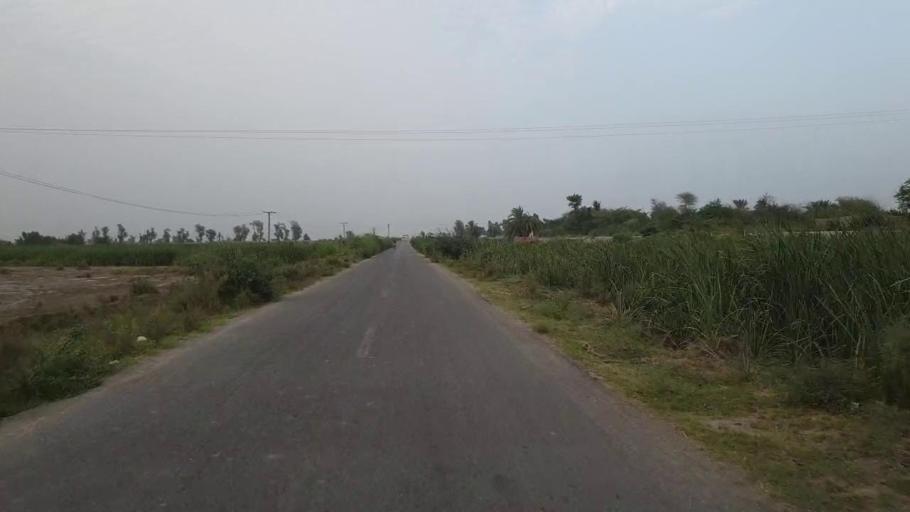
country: PK
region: Sindh
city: Daur
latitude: 26.4545
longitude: 68.2927
